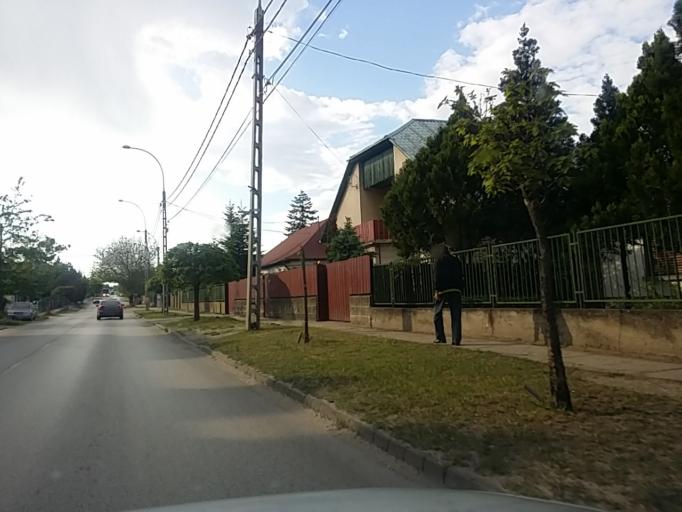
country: HU
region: Pest
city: Fot
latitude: 47.6297
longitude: 19.1780
